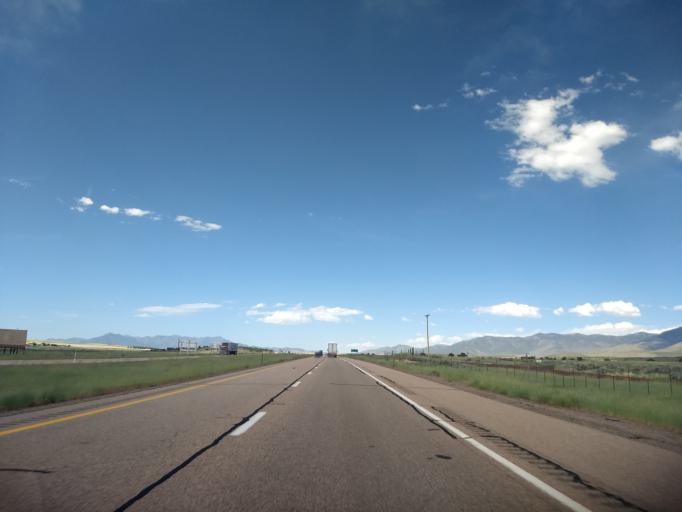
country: US
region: Utah
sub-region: Millard County
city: Fillmore
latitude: 39.0022
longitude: -112.3147
